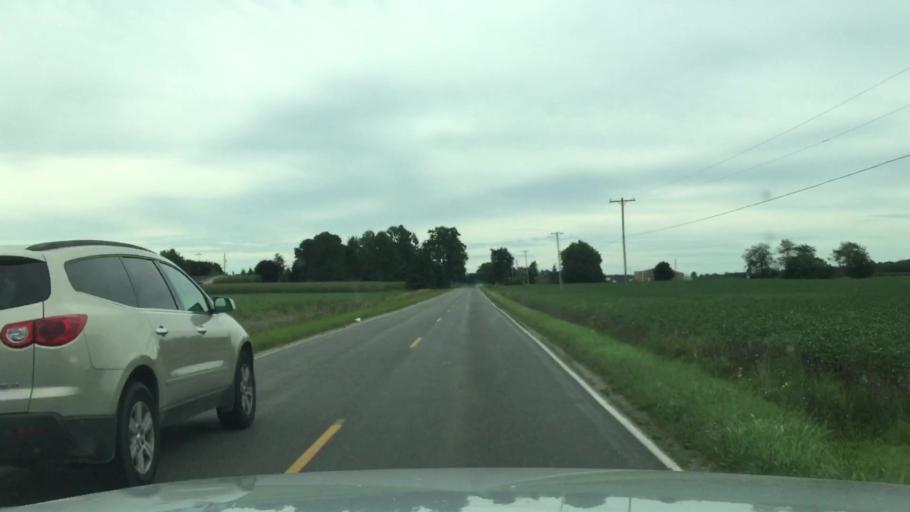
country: US
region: Michigan
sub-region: Shiawassee County
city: Durand
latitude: 43.0245
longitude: -83.9872
